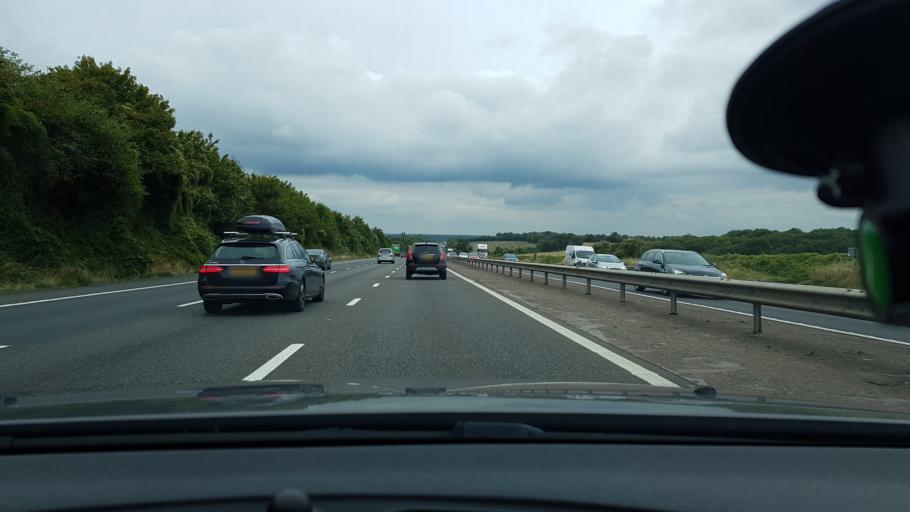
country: GB
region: England
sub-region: Hampshire
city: Basingstoke
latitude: 51.2334
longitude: -1.1183
